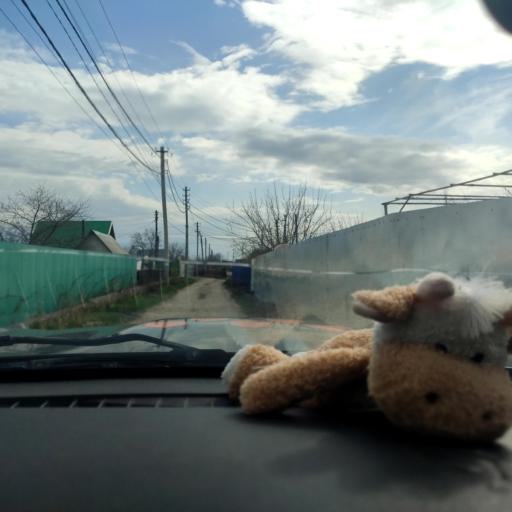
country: RU
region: Samara
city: Podstepki
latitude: 53.5938
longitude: 49.2248
